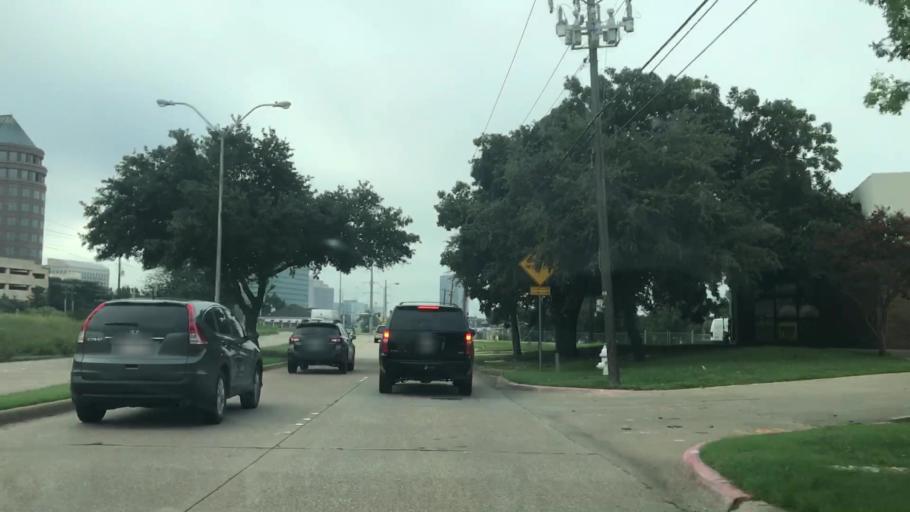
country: US
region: Texas
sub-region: Dallas County
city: Addison
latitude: 32.9418
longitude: -96.8263
